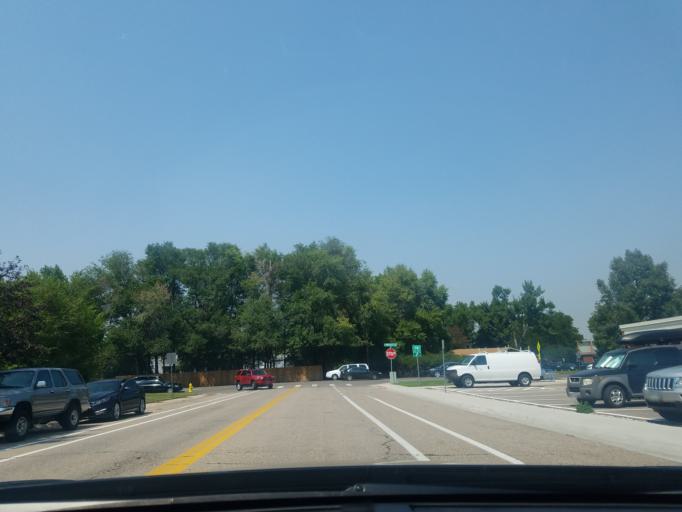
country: US
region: Colorado
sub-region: Larimer County
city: Fort Collins
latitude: 40.5665
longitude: -105.0675
